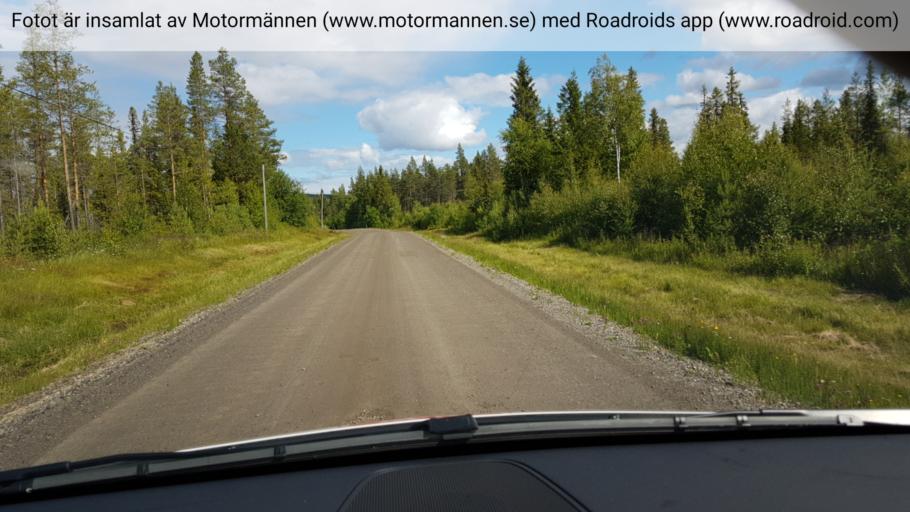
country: SE
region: Vaesterbotten
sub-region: Dorotea Kommun
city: Dorotea
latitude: 64.0936
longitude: 16.4698
